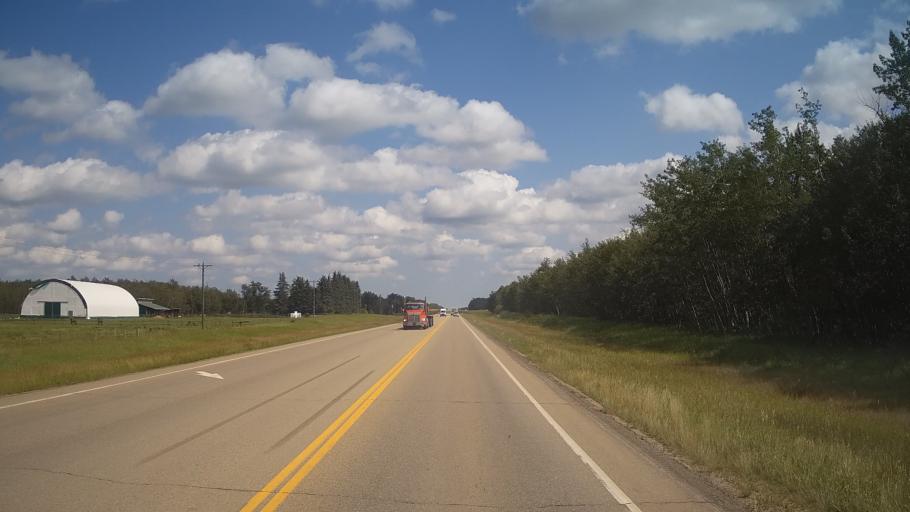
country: CA
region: Alberta
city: Sherwood Park
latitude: 53.3957
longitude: -113.0696
